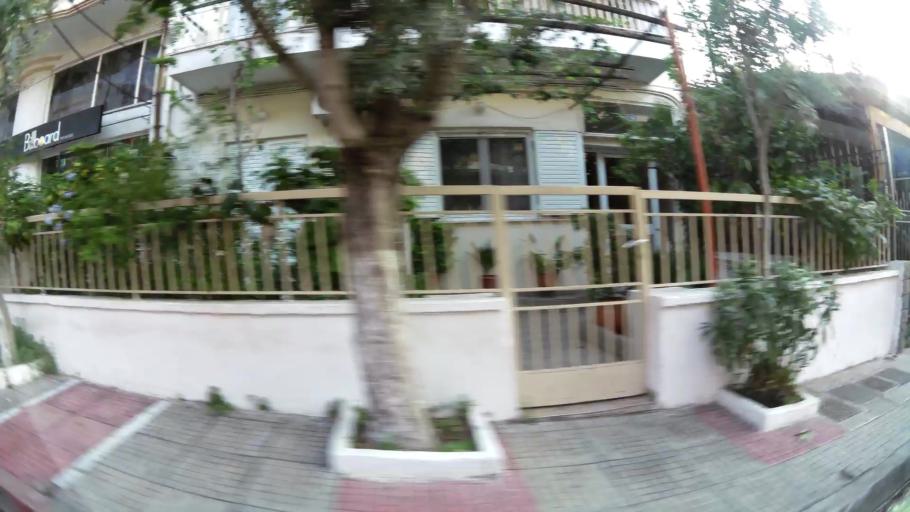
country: GR
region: Attica
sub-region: Nomarchia Athinas
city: Petroupolis
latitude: 38.0308
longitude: 23.6830
